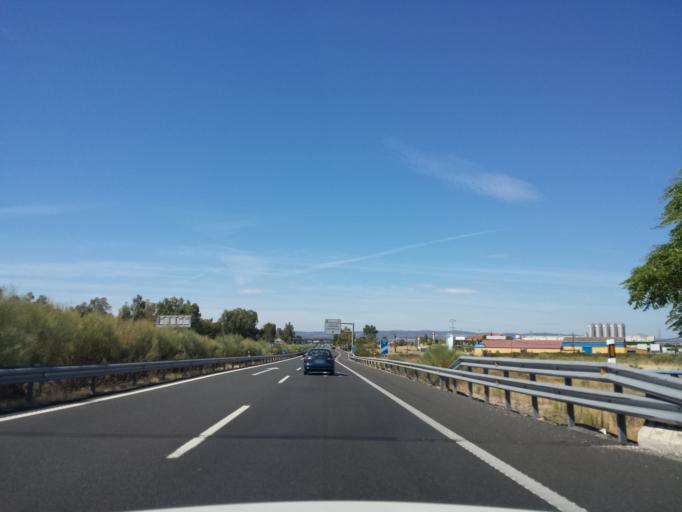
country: ES
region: Extremadura
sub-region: Provincia de Caceres
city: Millanes
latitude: 39.8539
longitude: -5.6218
